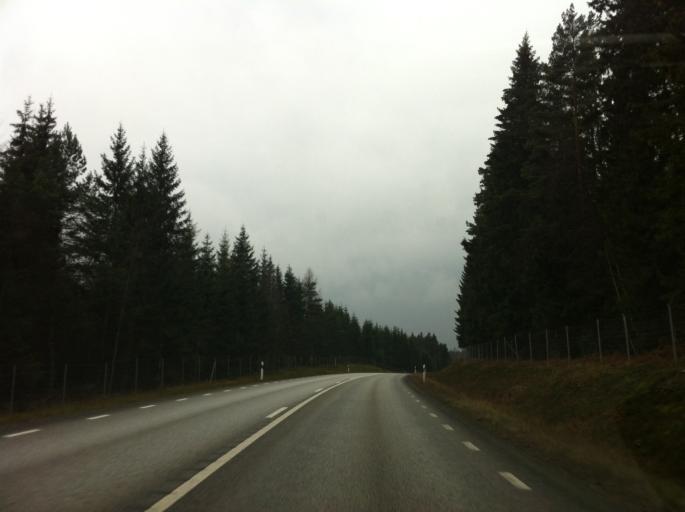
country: SE
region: Joenkoeping
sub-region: Savsjo Kommun
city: Saevsjoe
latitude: 57.3954
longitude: 14.6729
